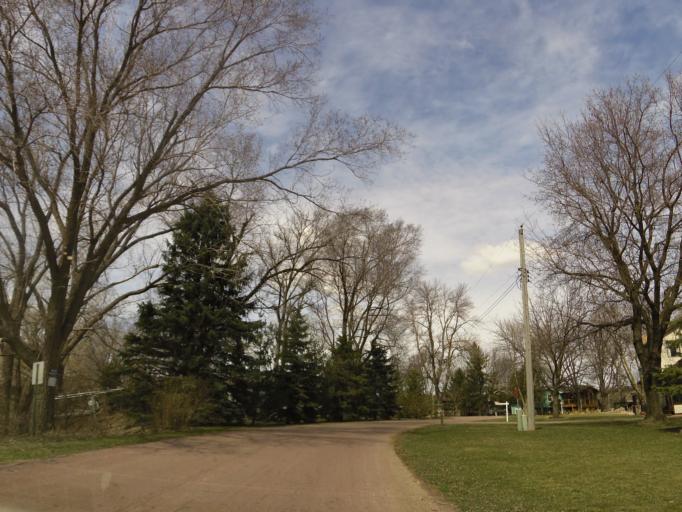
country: US
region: Minnesota
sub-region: Goodhue County
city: Cannon Falls
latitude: 44.5180
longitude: -92.9530
